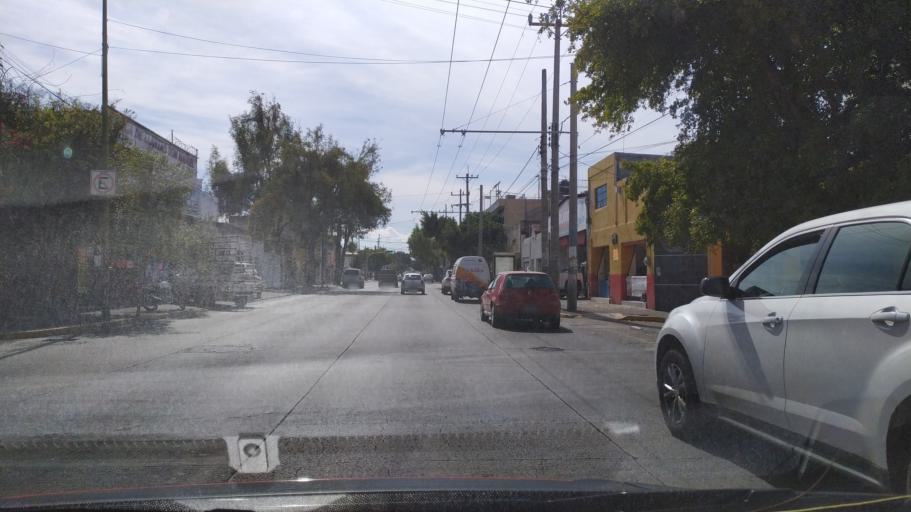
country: MX
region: Jalisco
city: Tlaquepaque
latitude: 20.6766
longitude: -103.3291
